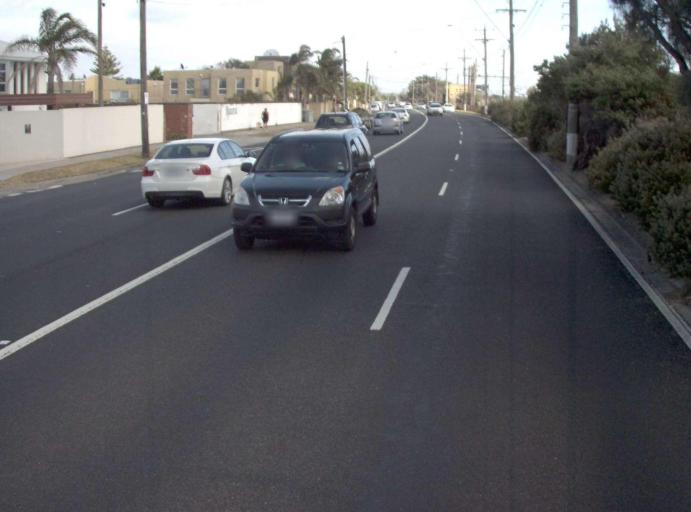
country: AU
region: Victoria
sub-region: Kingston
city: Aspendale
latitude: -38.0183
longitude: 145.0958
